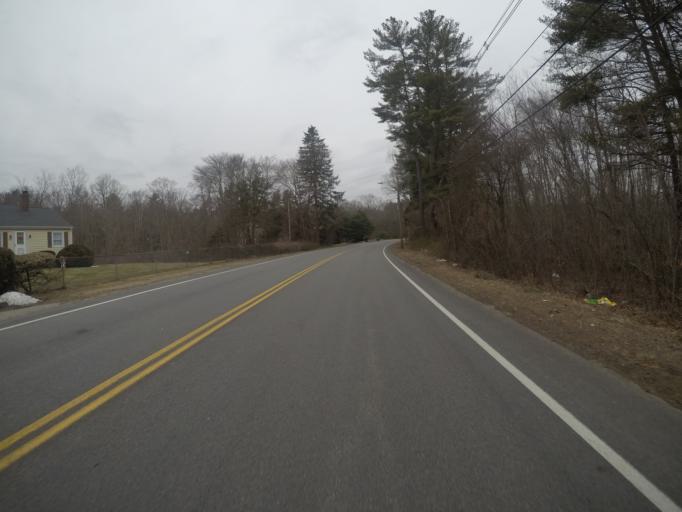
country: US
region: Massachusetts
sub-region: Bristol County
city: Easton
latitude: 42.0132
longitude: -71.0880
